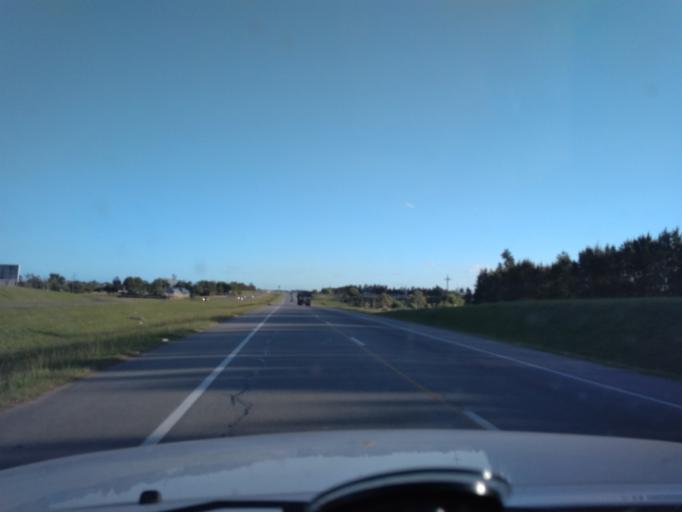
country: UY
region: Canelones
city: Las Piedras
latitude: -34.7327
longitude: -56.2494
